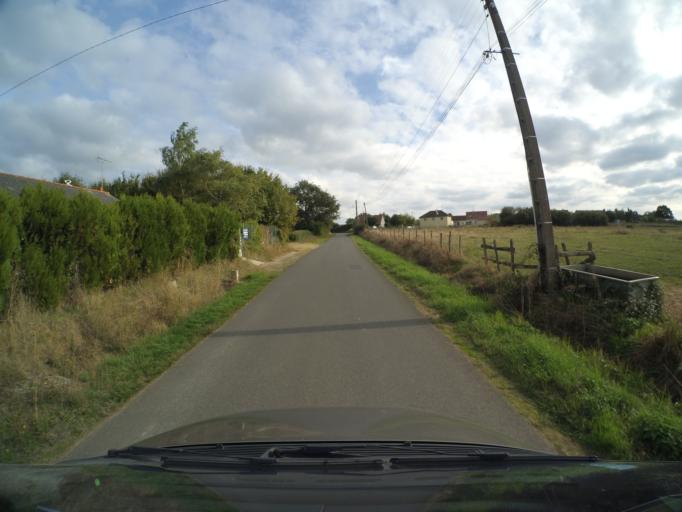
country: FR
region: Centre
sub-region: Departement d'Indre-et-Loire
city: Poce-sur-Cisse
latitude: 47.4743
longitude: 0.9656
